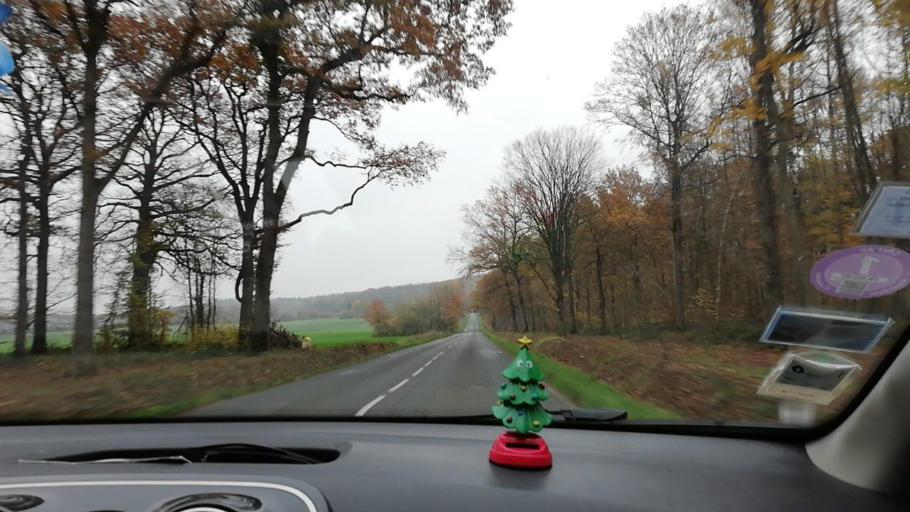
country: FR
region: Ile-de-France
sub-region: Departement de Seine-et-Marne
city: Saint-Mard
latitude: 49.0382
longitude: 2.7296
